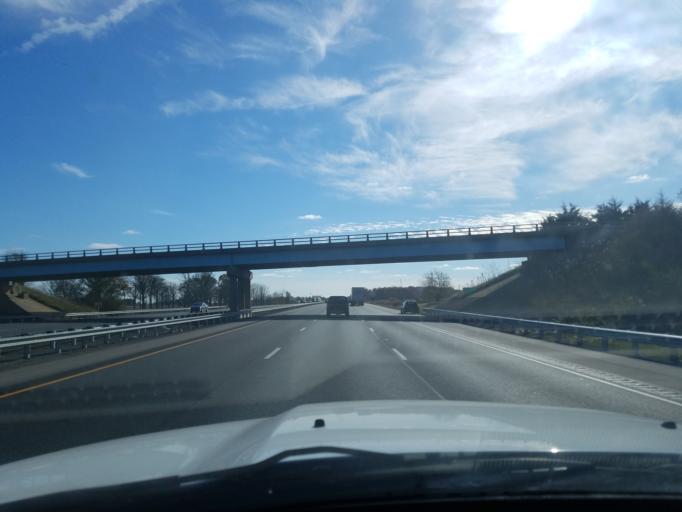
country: US
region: Indiana
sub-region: Johnson County
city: Franklin
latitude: 39.5220
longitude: -86.0248
